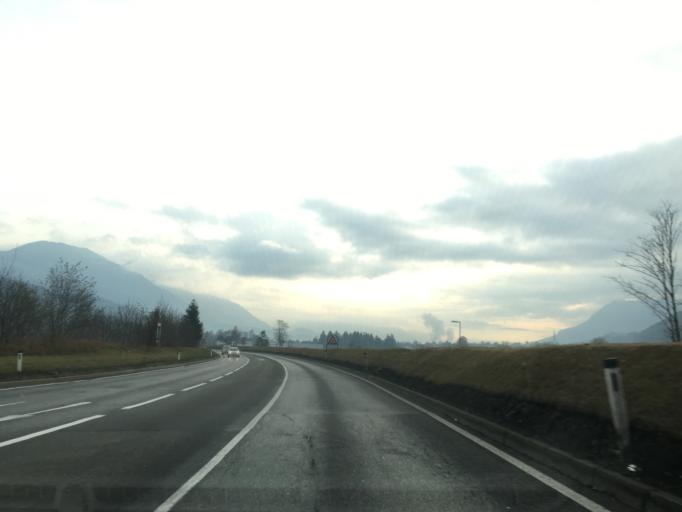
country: AT
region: Vorarlberg
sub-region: Politischer Bezirk Feldkirch
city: Feldkirch
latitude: 47.2248
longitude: 9.6092
